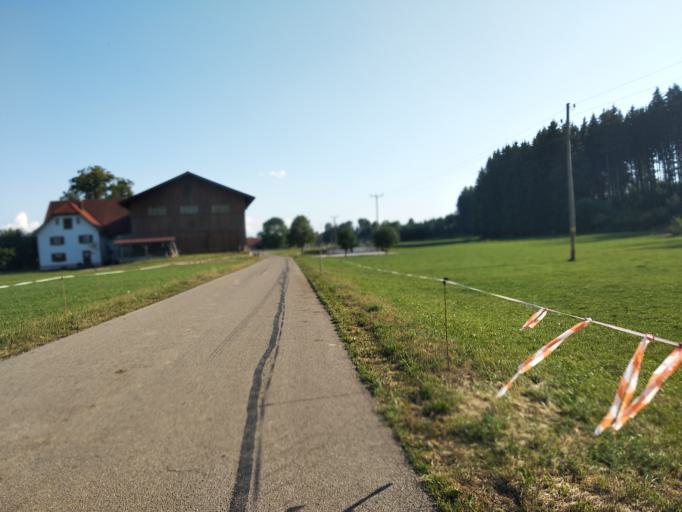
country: DE
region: Bavaria
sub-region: Swabia
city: Lautrach
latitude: 47.8758
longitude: 10.1182
